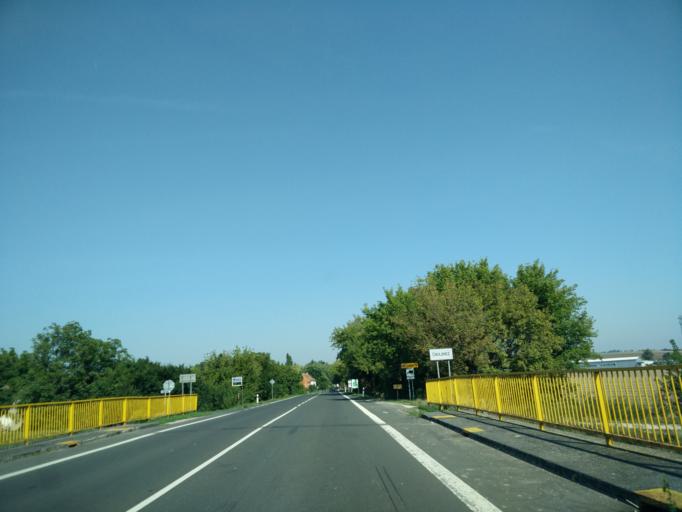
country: SK
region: Nitriansky
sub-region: Okres Nitra
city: Nitra
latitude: 48.3691
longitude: 18.0429
